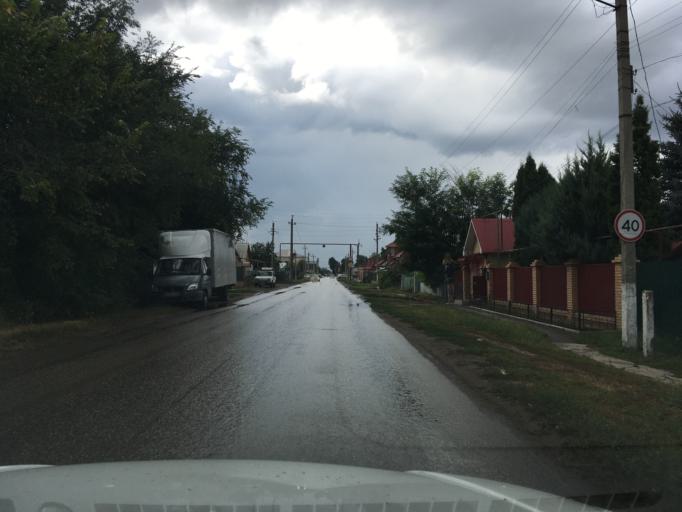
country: RU
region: Samara
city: Bezenchuk
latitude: 52.9801
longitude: 49.4367
